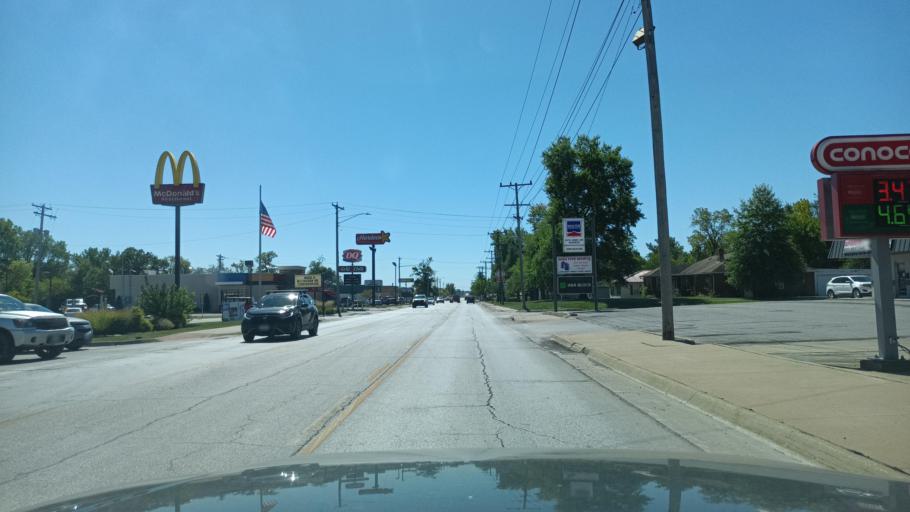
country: US
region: Missouri
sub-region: Adair County
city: Kirksville
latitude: 40.1849
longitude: -92.5720
